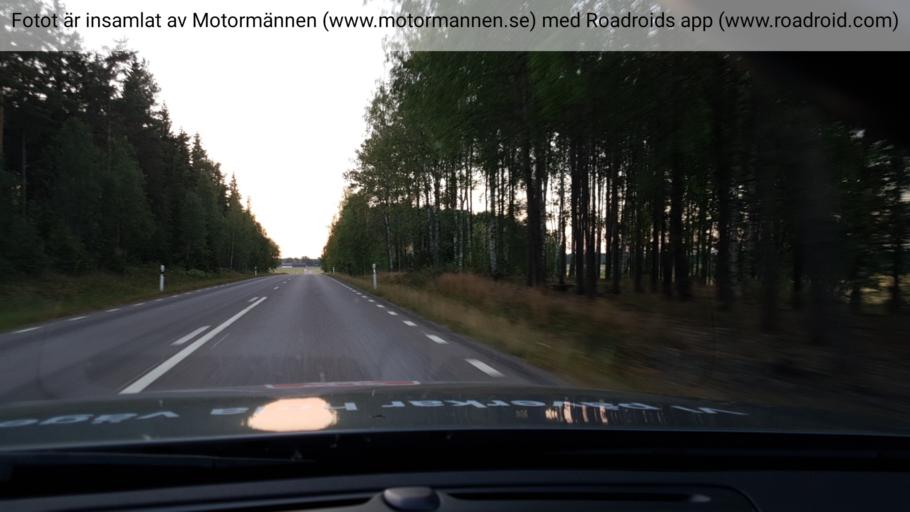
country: SE
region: Uppsala
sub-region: Heby Kommun
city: OEstervala
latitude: 60.0852
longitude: 17.1909
